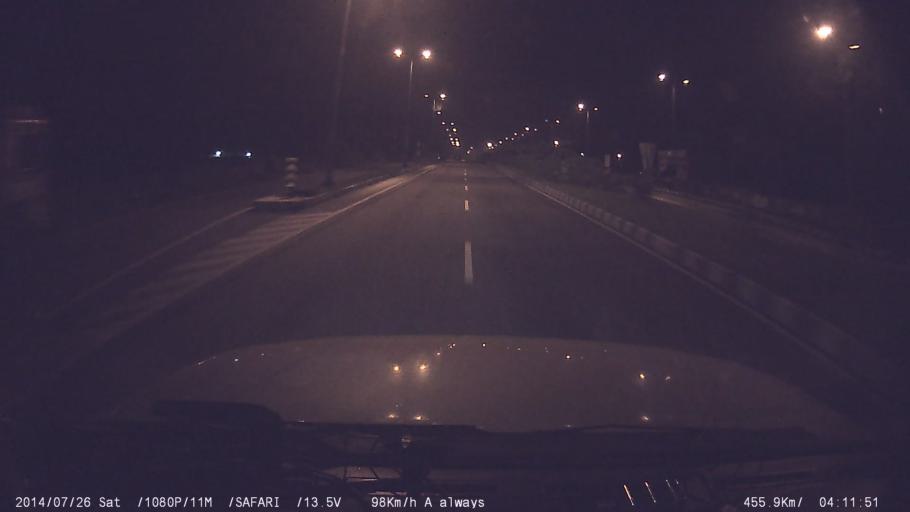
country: IN
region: Kerala
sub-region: Thrissur District
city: Trichur
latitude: 10.5005
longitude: 76.2582
